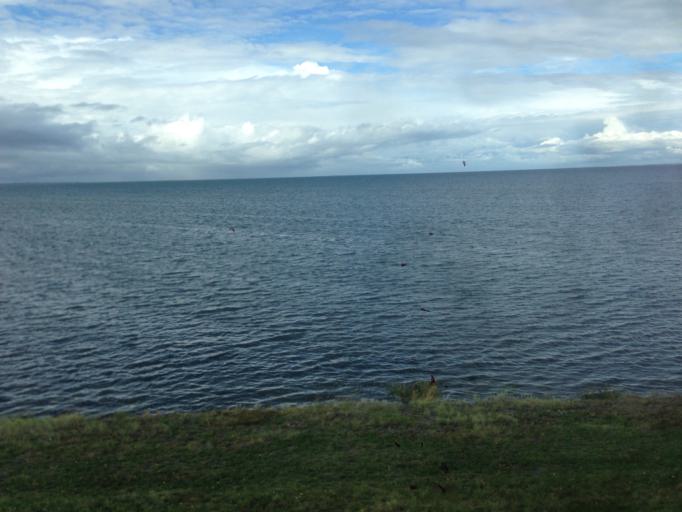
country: DE
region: Schleswig-Holstein
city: Friedrich-Wilhelm-Lubke-Koog
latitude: 54.8842
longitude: 8.5433
